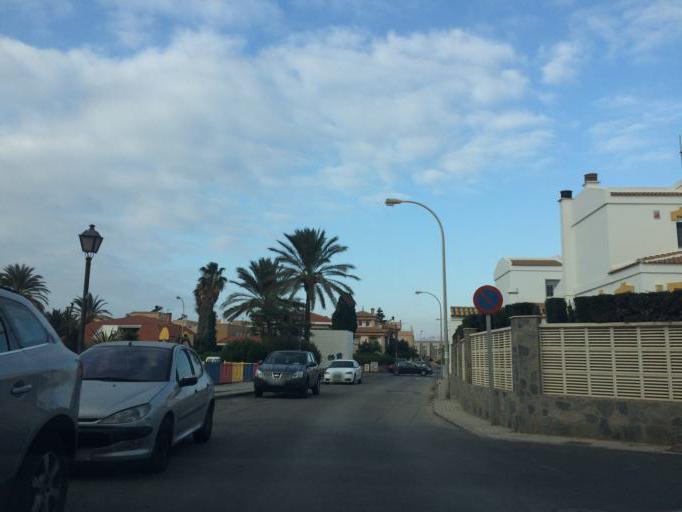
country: ES
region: Andalusia
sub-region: Provincia de Almeria
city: Almeria
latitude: 36.8196
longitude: -2.4362
